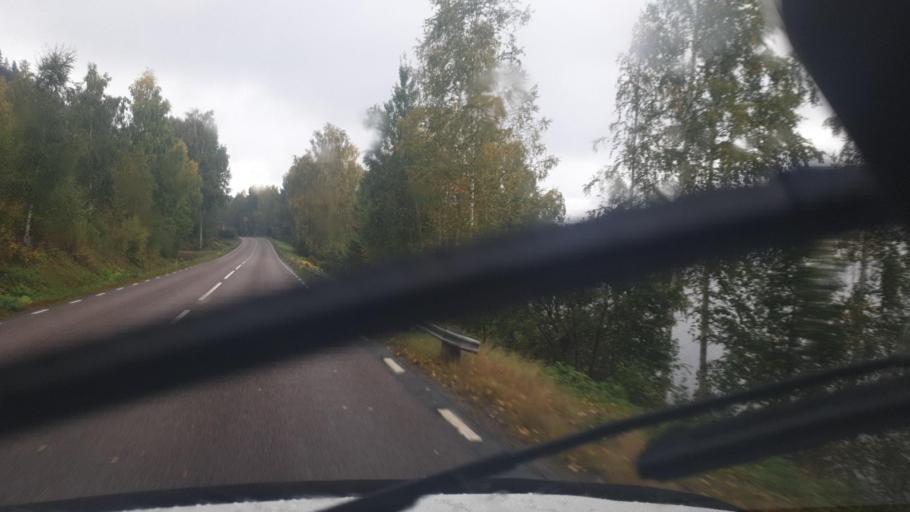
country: SE
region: Vaermland
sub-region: Sunne Kommun
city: Sunne
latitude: 59.8158
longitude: 13.0145
